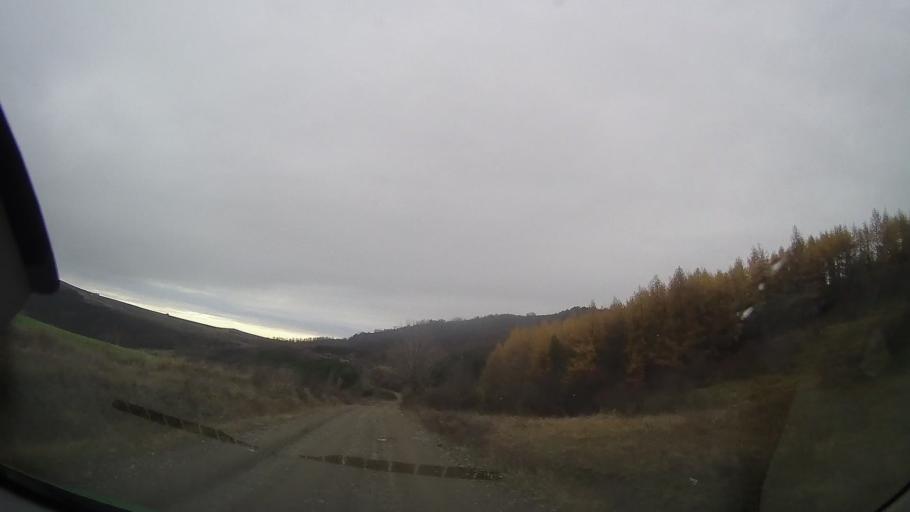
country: RO
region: Mures
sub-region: Comuna Bala
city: Bala
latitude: 46.6775
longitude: 24.4853
